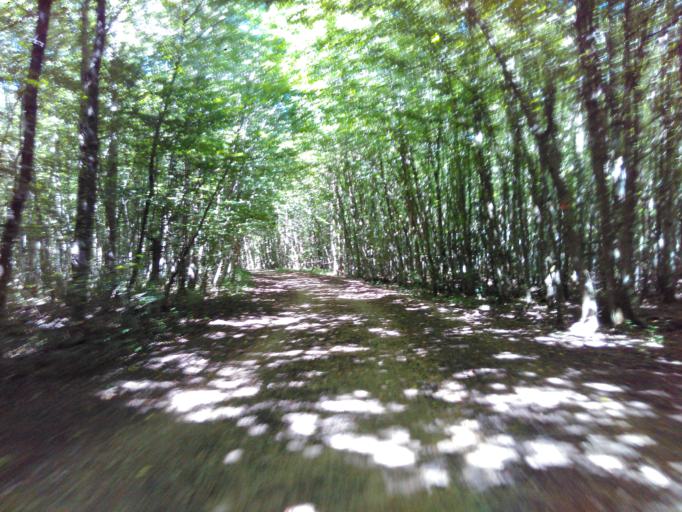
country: LU
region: Luxembourg
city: Bergem
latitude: 49.5378
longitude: 6.0686
